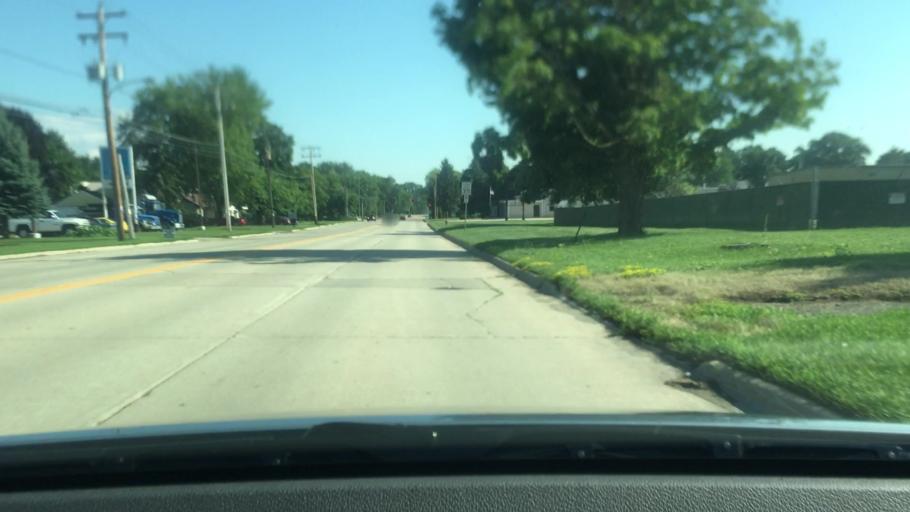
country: US
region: Wisconsin
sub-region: Winnebago County
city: Oshkosh
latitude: 43.9835
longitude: -88.5426
